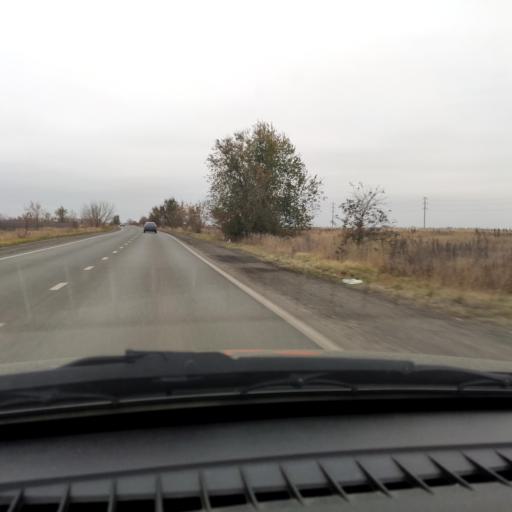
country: RU
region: Samara
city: Podstepki
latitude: 53.5177
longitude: 49.2112
